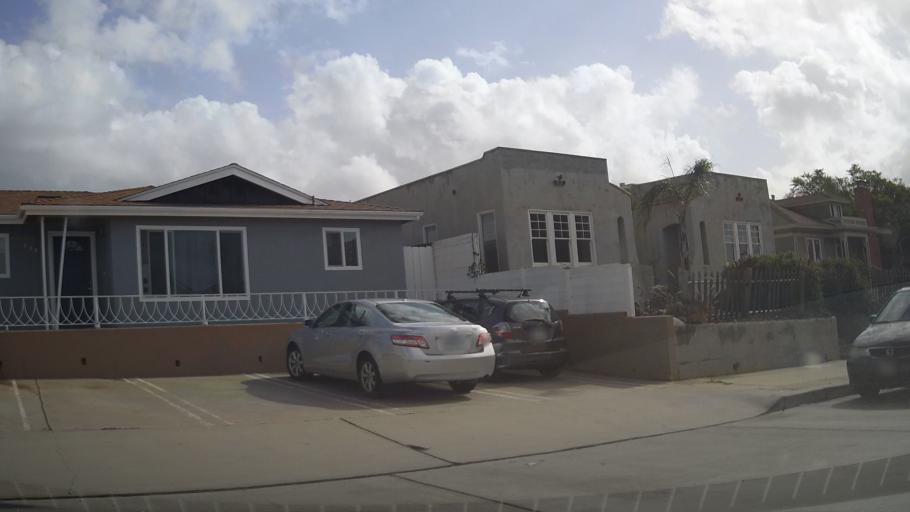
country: US
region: California
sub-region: San Diego County
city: San Diego
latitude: 32.7144
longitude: -117.1382
